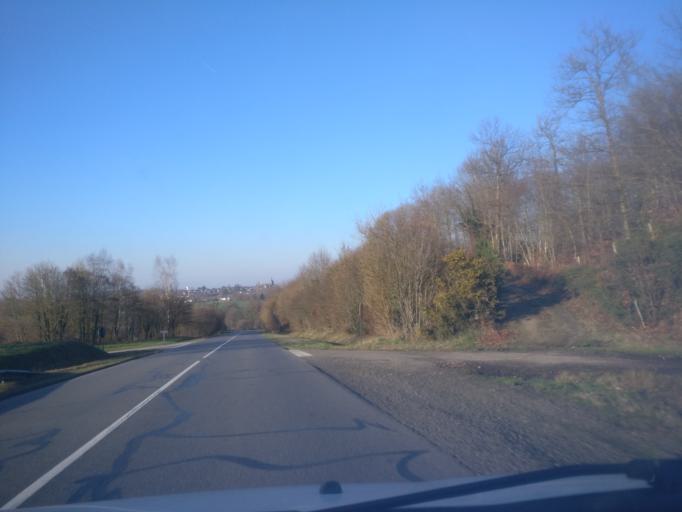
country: FR
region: Brittany
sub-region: Departement d'Ille-et-Vilaine
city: Livre-sur-Changeon
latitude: 48.2075
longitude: -1.3361
